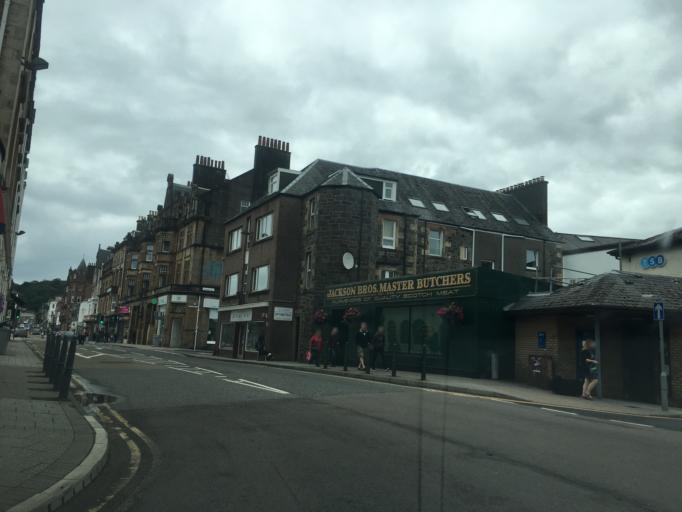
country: GB
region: Scotland
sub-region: Argyll and Bute
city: Oban
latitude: 56.4127
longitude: -5.4722
